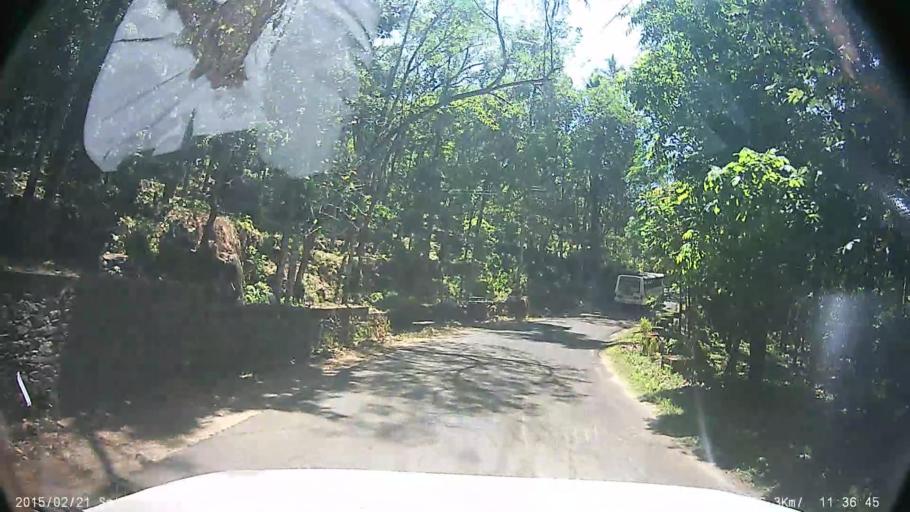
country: IN
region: Kerala
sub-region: Kottayam
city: Lalam
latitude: 9.8119
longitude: 76.7282
